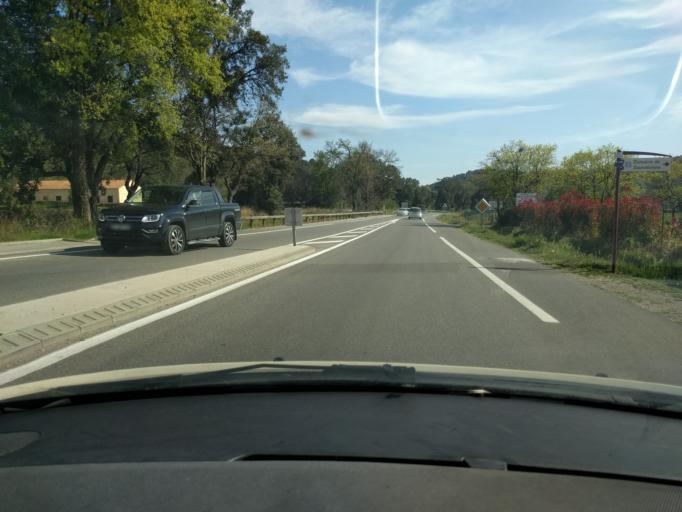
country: FR
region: Provence-Alpes-Cote d'Azur
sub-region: Departement du Var
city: La Crau
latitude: 43.1721
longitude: 6.1181
